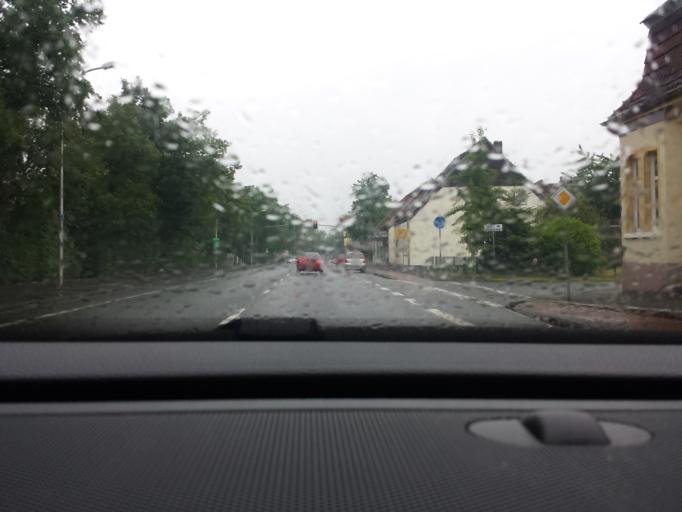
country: DE
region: North Rhine-Westphalia
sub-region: Regierungsbezirk Munster
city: Gronau
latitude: 52.2139
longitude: 7.0015
